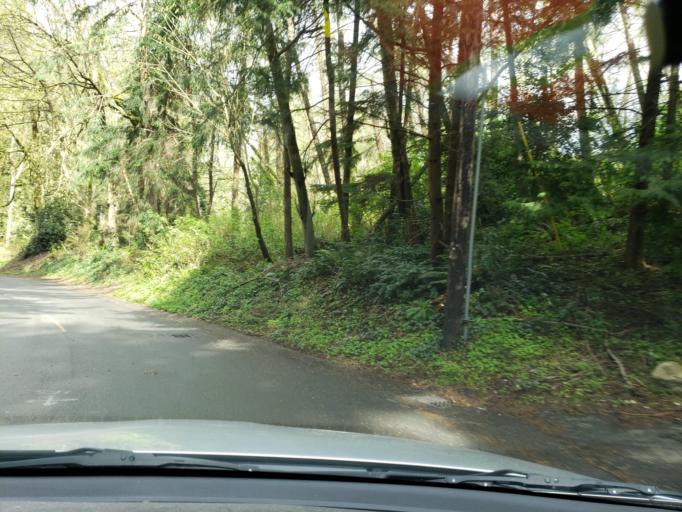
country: US
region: Washington
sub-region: Snohomish County
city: Meadowdale
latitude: 47.8359
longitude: -122.3444
